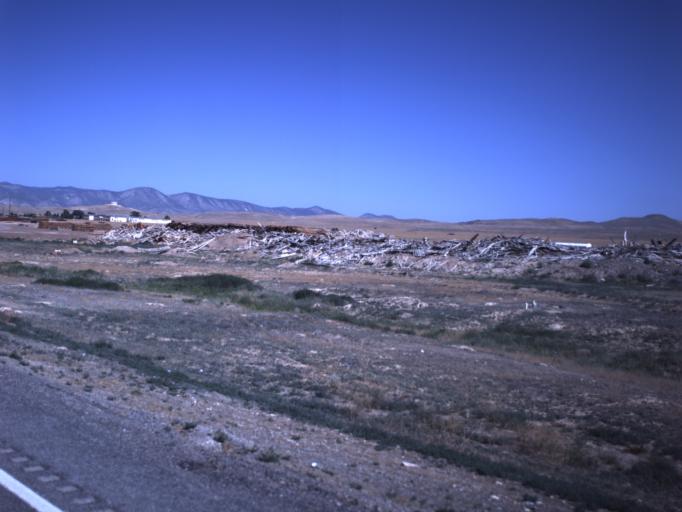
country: US
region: Utah
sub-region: Sanpete County
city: Gunnison
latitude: 39.1614
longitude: -111.7911
